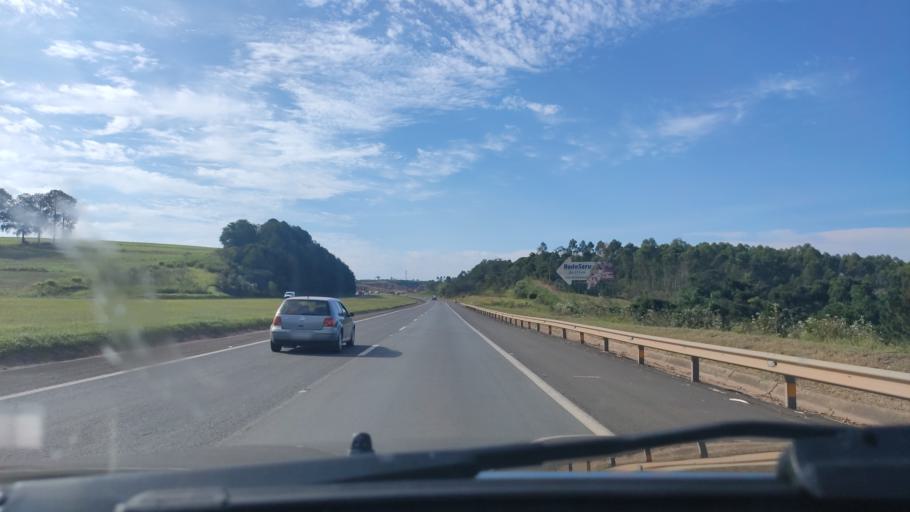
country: BR
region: Sao Paulo
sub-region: Itatinga
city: Itatinga
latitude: -23.1310
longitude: -48.4671
